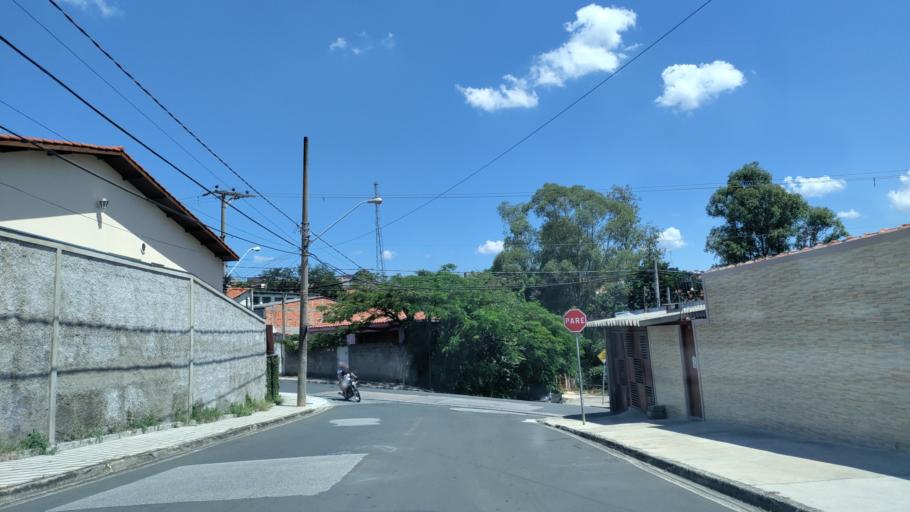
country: BR
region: Sao Paulo
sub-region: Sorocaba
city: Sorocaba
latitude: -23.4716
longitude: -47.4651
